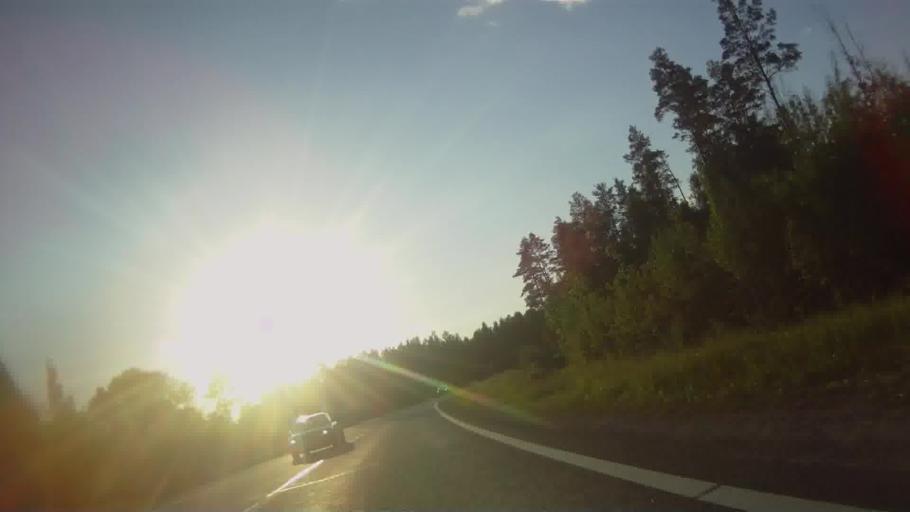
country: LV
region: Livani
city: Livani
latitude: 56.5302
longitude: 26.1438
